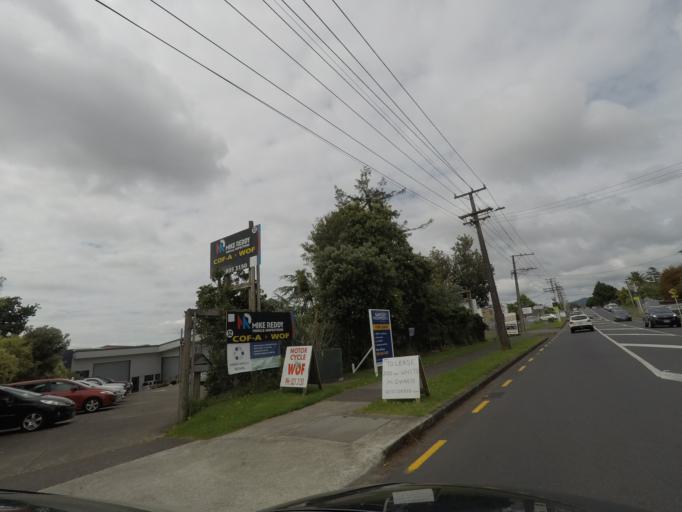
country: NZ
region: Auckland
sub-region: Auckland
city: Waitakere
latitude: -36.8939
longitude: 174.6289
